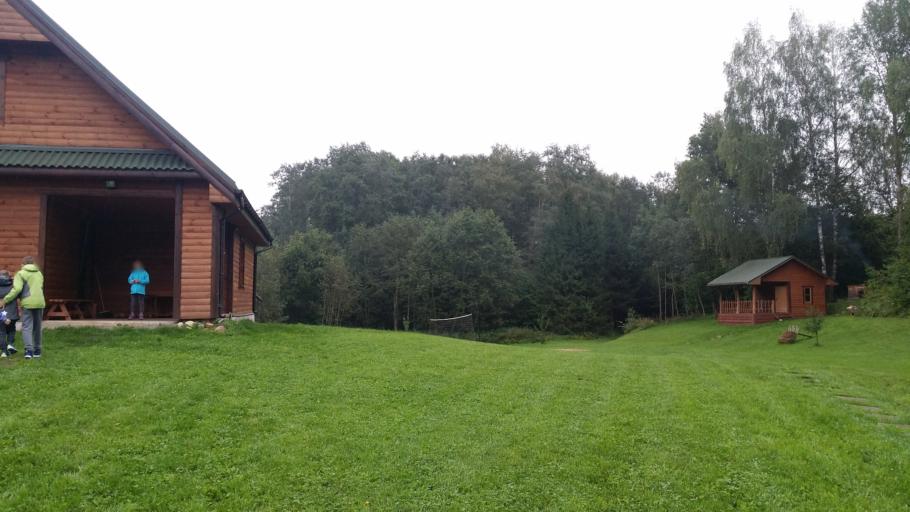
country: LT
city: Moletai
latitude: 55.3440
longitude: 25.3895
